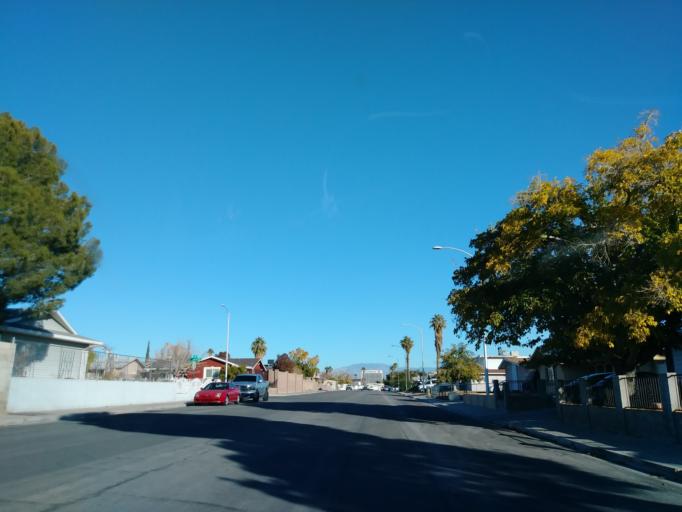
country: US
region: Nevada
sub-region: Clark County
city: Spring Valley
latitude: 36.1639
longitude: -115.2469
